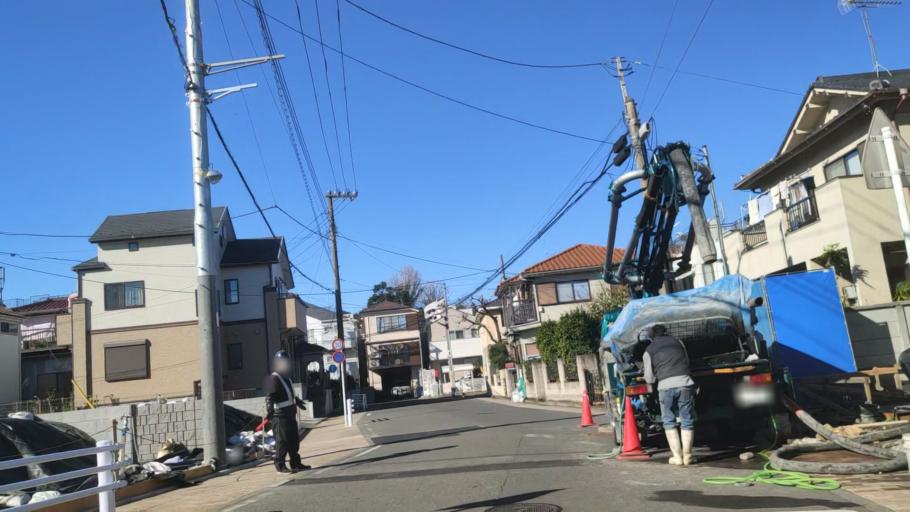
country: JP
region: Kanagawa
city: Yokohama
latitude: 35.4290
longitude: 139.6597
